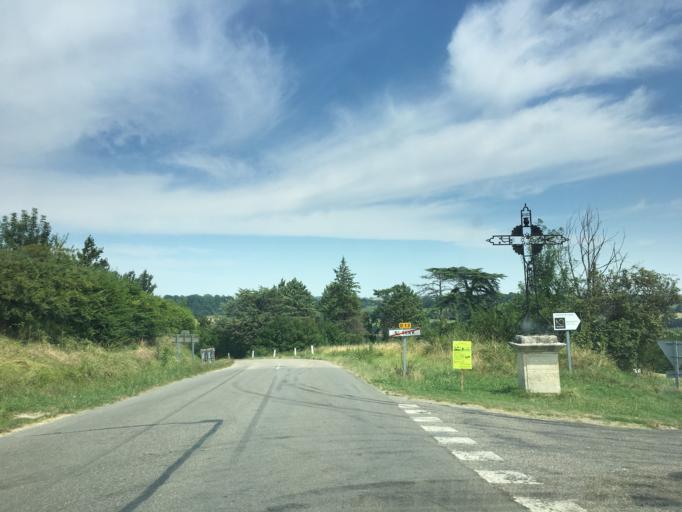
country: FR
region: Midi-Pyrenees
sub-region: Departement du Gers
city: Fleurance
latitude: 43.8909
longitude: 0.7727
